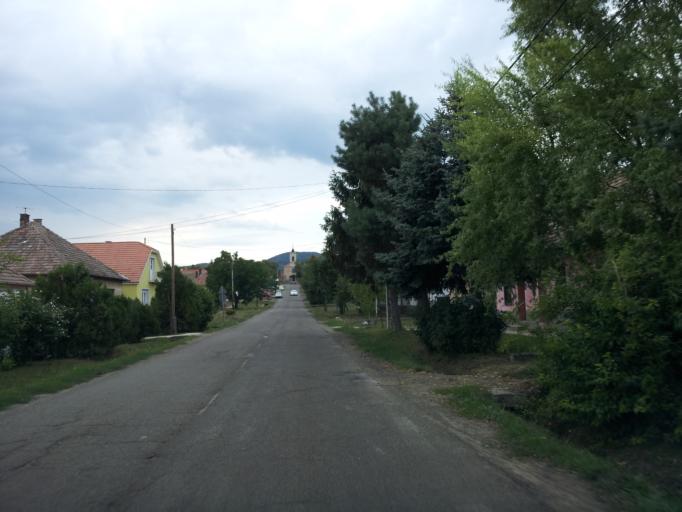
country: HU
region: Pest
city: Kismaros
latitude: 47.8757
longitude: 18.9351
